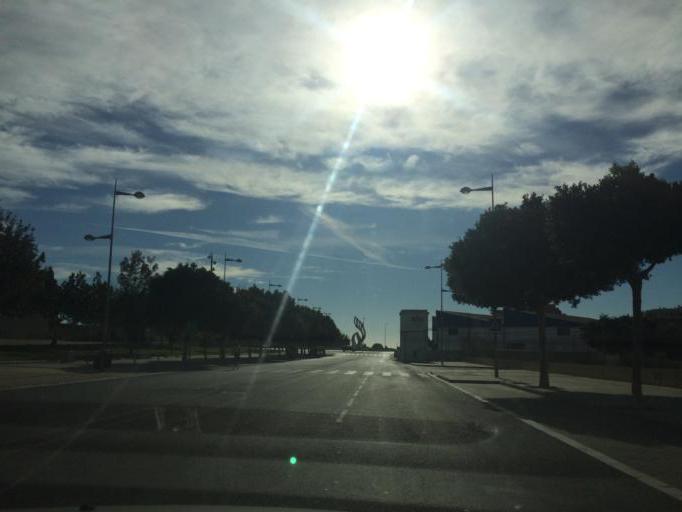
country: ES
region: Andalusia
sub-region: Provincia de Almeria
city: Almeria
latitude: 36.8384
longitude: -2.4396
